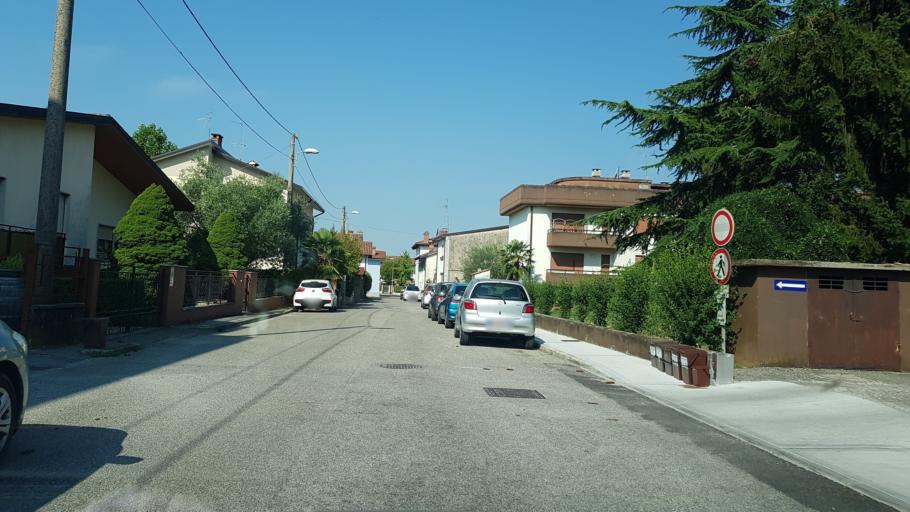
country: IT
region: Friuli Venezia Giulia
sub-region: Provincia di Gorizia
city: Mossa
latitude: 45.9369
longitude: 13.5491
